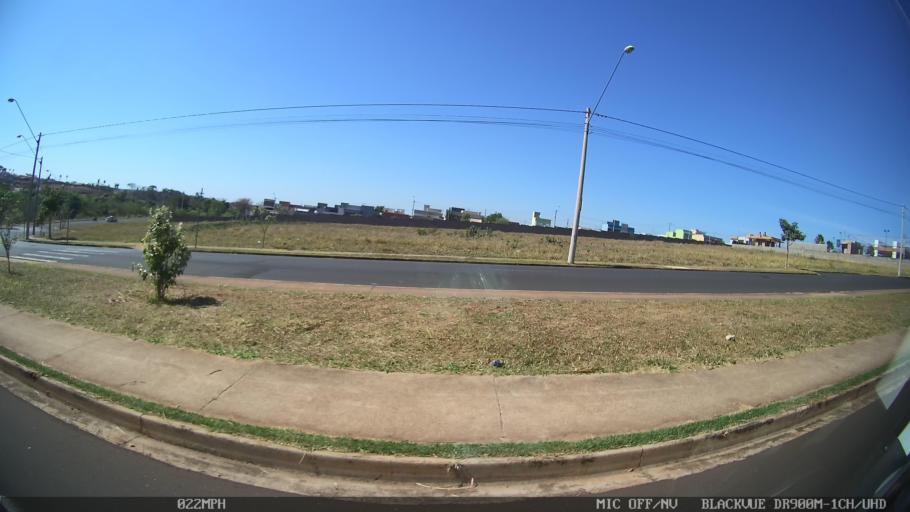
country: BR
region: Sao Paulo
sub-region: Sao Jose Do Rio Preto
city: Sao Jose do Rio Preto
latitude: -20.7630
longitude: -49.4201
